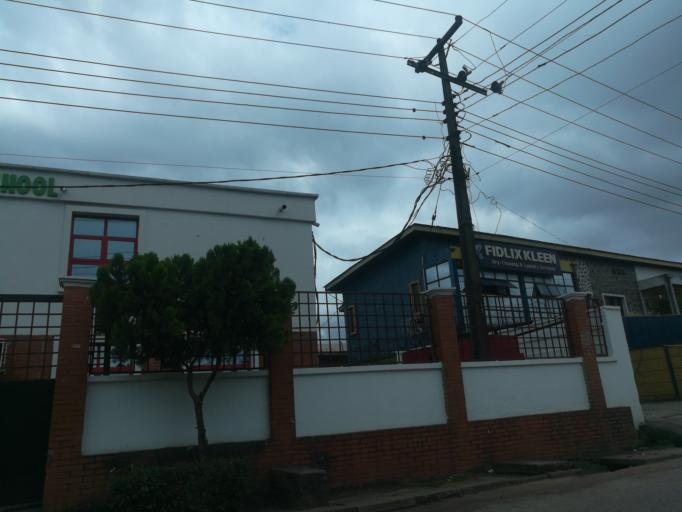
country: NG
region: Lagos
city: Somolu
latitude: 6.5550
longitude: 3.3623
